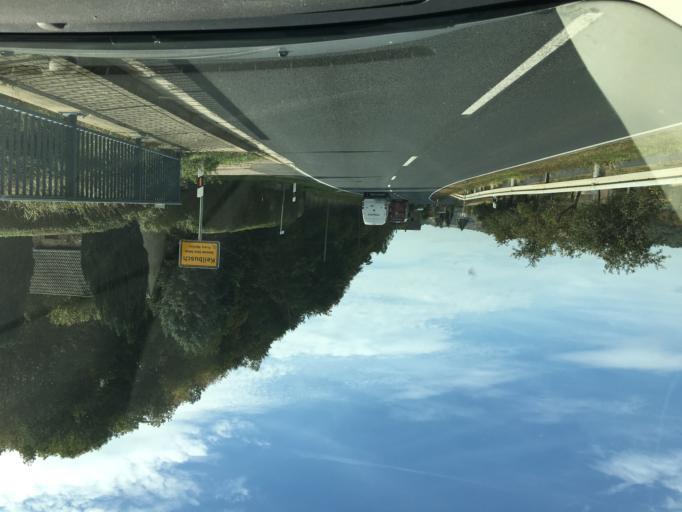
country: DE
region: Saxony
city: Meissen
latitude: 51.1885
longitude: 13.4291
